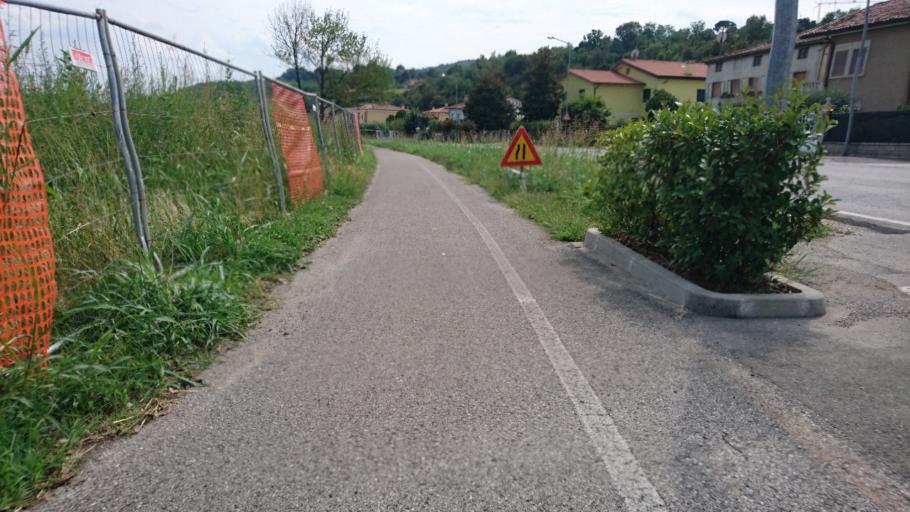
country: IT
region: Veneto
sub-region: Provincia di Vicenza
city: Longare
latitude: 45.4949
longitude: 11.5903
